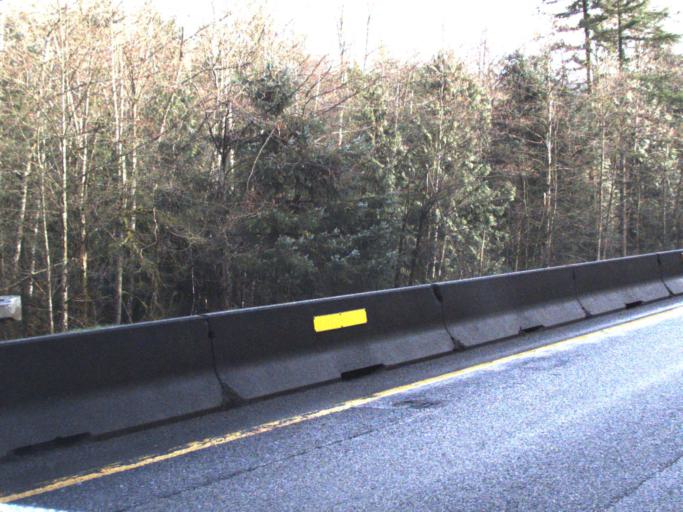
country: US
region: Washington
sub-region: King County
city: Hobart
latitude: 47.4632
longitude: -121.9420
